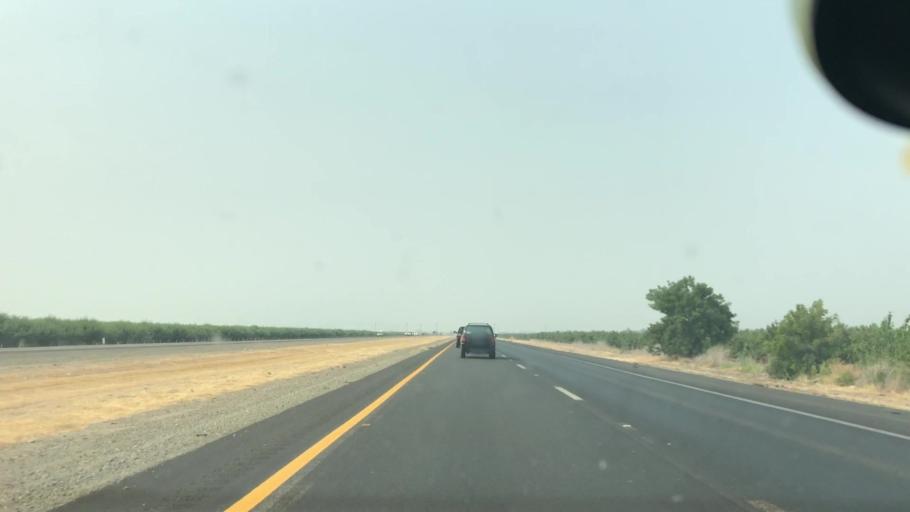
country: US
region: California
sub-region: San Joaquin County
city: Tracy
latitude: 37.7246
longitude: -121.3434
